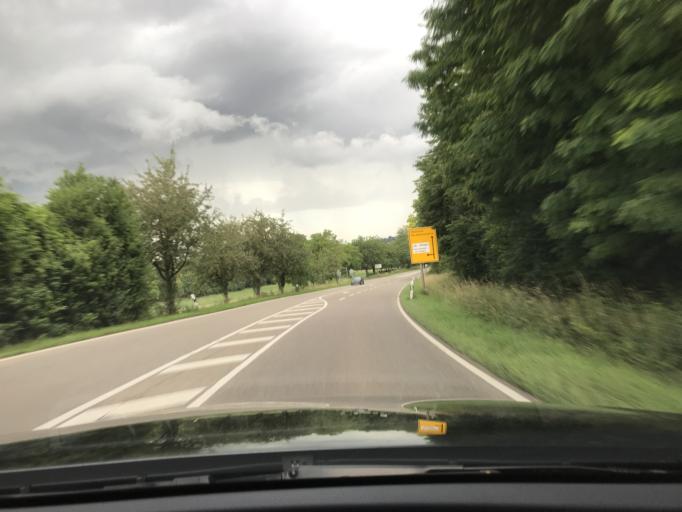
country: DE
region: Baden-Wuerttemberg
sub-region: Regierungsbezirk Stuttgart
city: Stuttgart Muehlhausen
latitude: 48.8664
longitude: 9.2655
